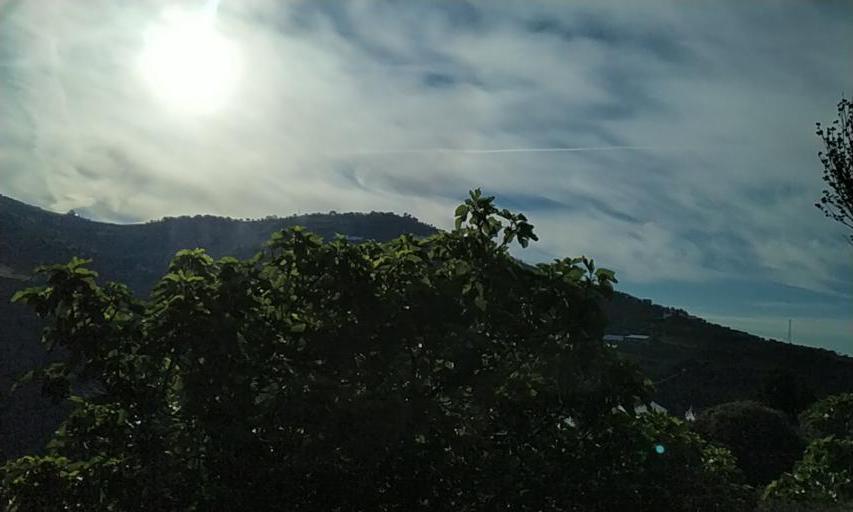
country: PT
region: Vila Real
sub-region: Sabrosa
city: Vilela
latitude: 41.2039
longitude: -7.5467
